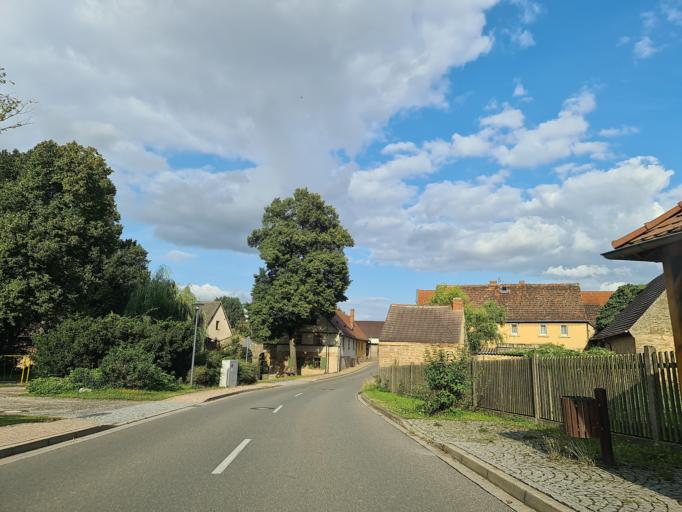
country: DE
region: Saxony-Anhalt
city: Droyssig
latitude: 51.0400
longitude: 12.0073
